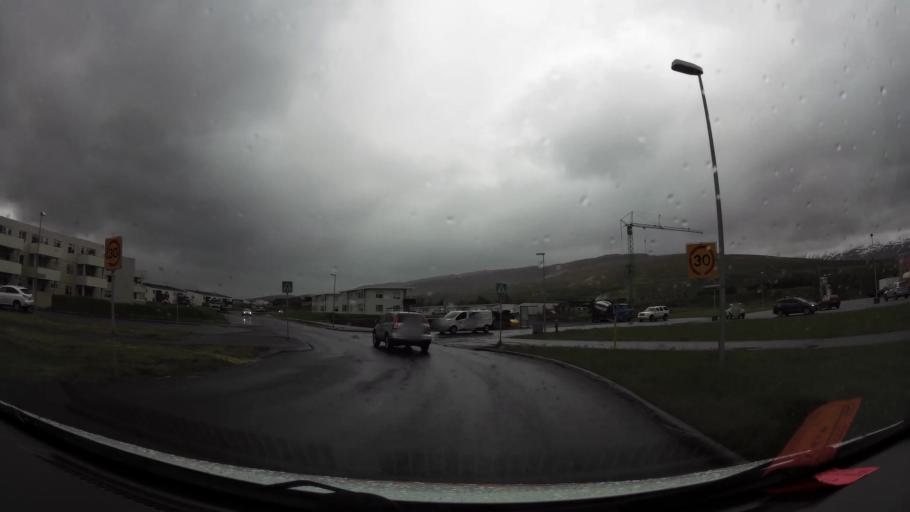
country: IS
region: Northeast
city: Akureyri
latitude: 65.6692
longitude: -18.1086
